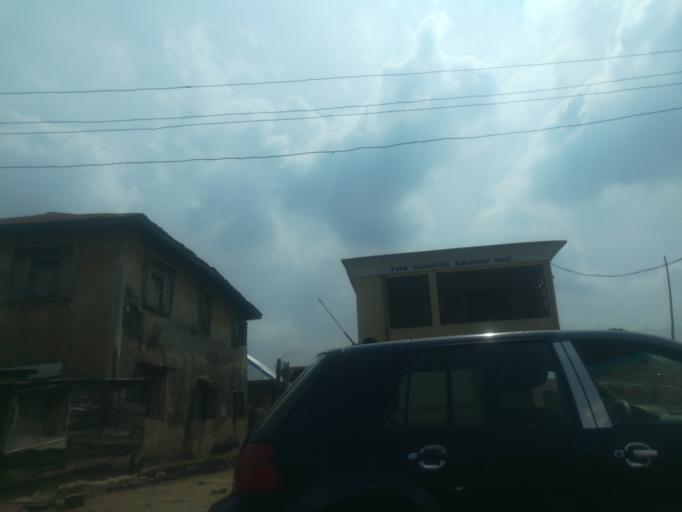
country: NG
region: Oyo
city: Ibadan
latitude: 7.3954
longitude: 3.9082
